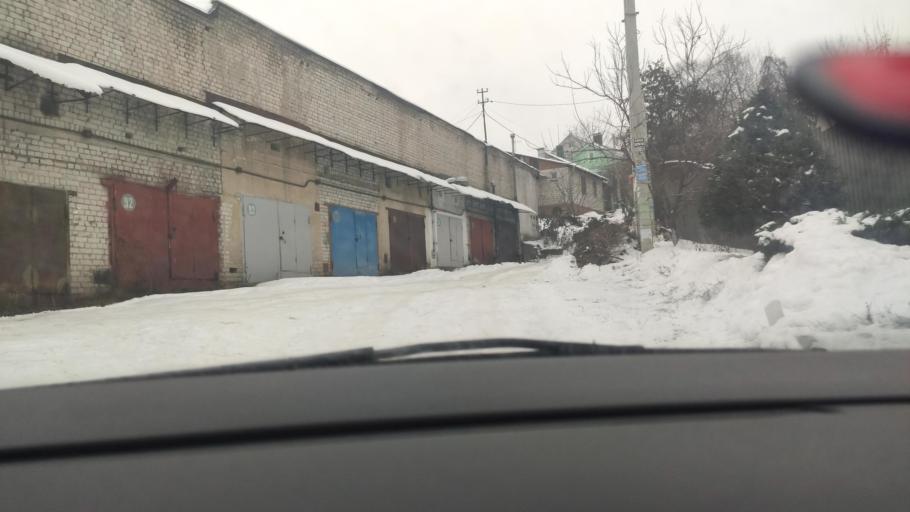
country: RU
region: Voronezj
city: Voronezh
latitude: 51.6364
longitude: 39.2003
